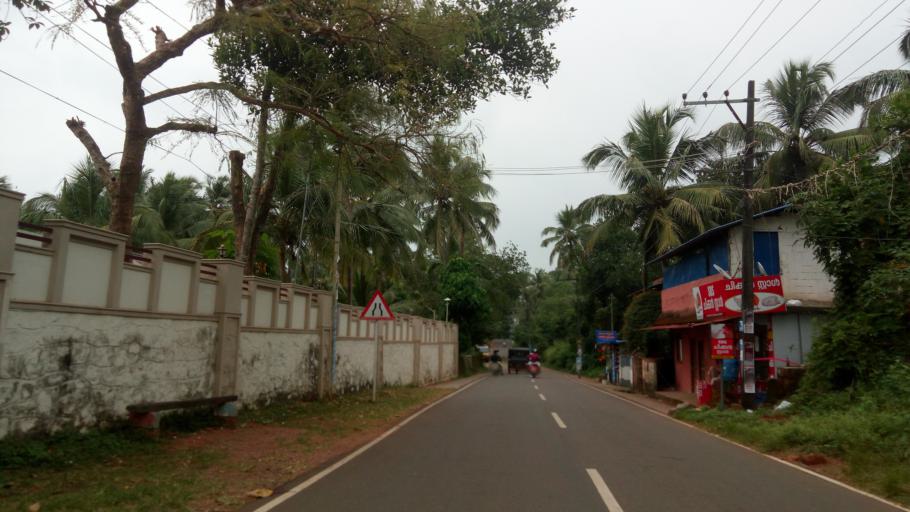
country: IN
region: Kerala
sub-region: Malappuram
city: Malappuram
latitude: 10.9856
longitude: 76.0072
